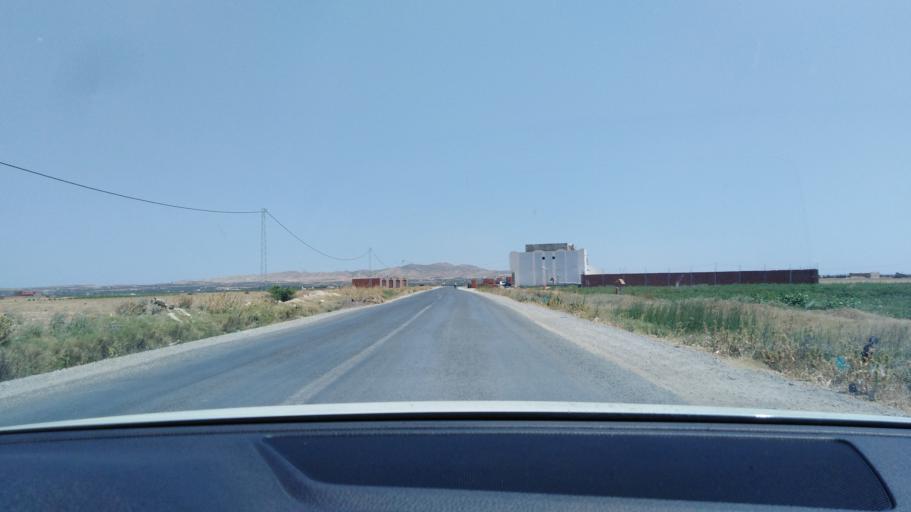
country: TN
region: Al Qayrawan
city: Sbikha
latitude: 36.1137
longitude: 10.1000
